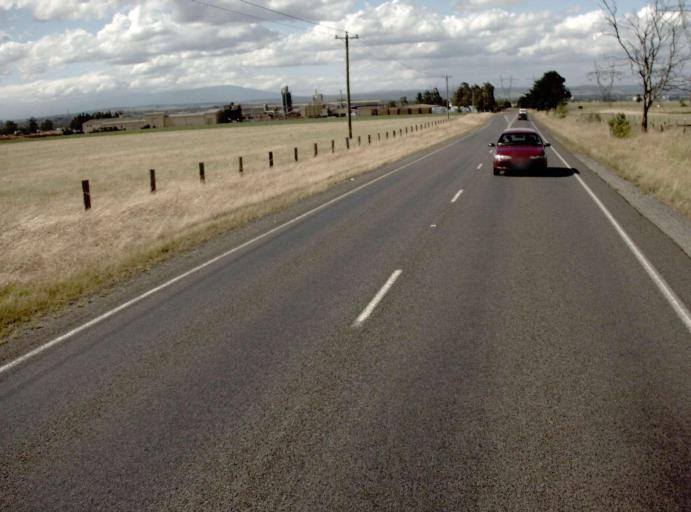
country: AU
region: Victoria
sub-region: Latrobe
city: Morwell
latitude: -38.2704
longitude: 146.4337
